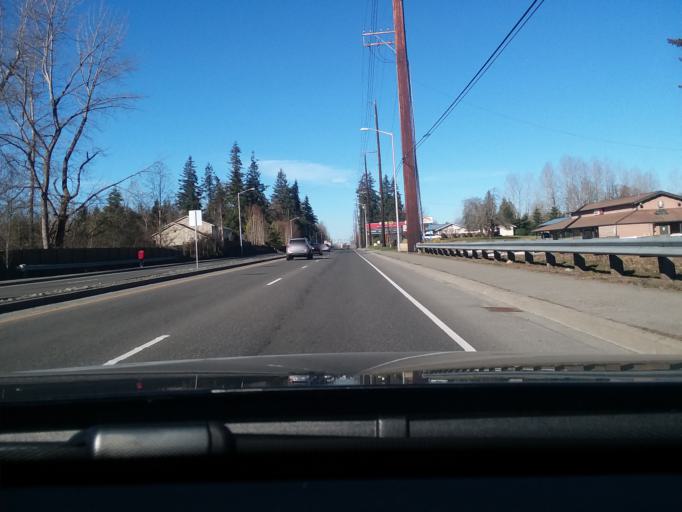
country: US
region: Washington
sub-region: Pierce County
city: Frederickson
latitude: 47.0966
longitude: -122.3372
